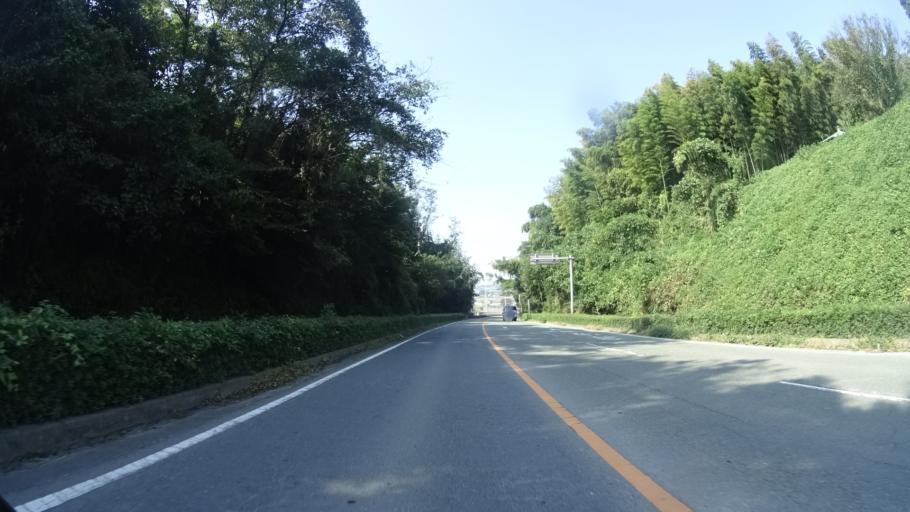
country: JP
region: Kumamoto
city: Ozu
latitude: 32.8512
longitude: 130.8569
